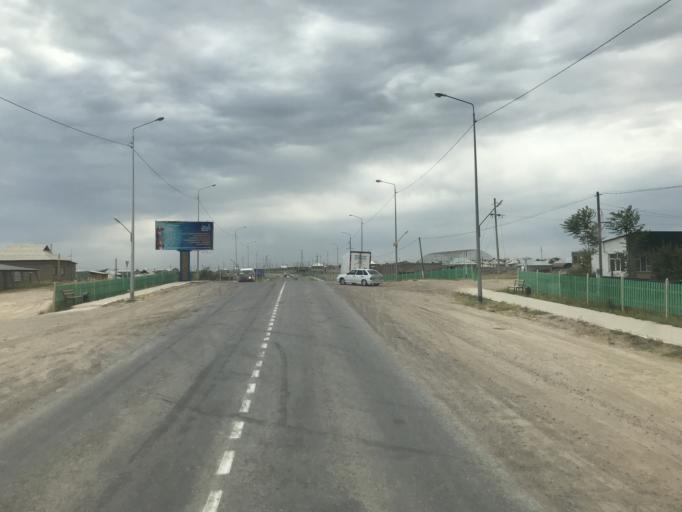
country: KZ
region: Ongtustik Qazaqstan
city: Saryaghash
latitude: 41.4299
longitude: 69.1043
